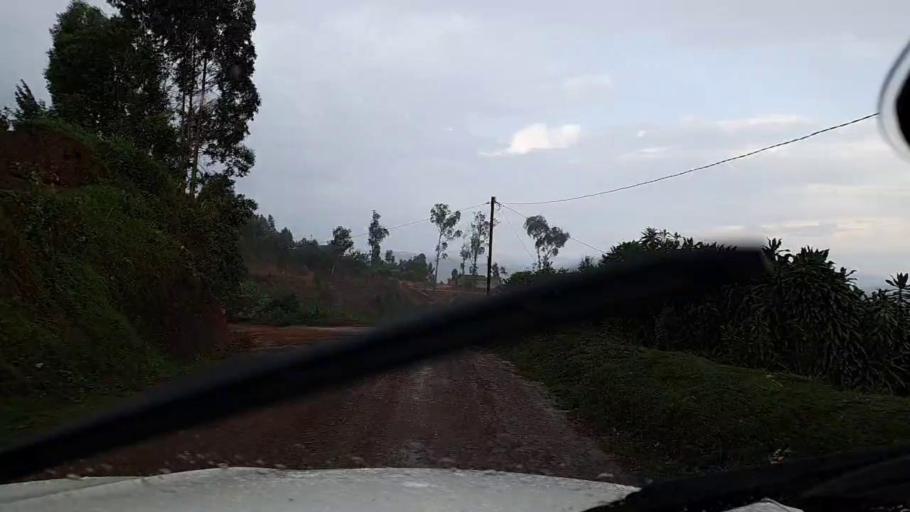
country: BI
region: Kayanza
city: Kayanza
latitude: -2.7782
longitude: 29.5355
